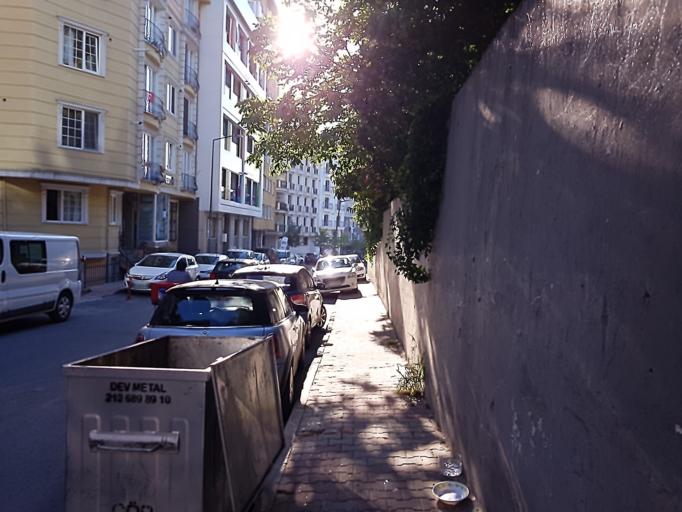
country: TR
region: Istanbul
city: Sisli
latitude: 41.0715
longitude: 29.0056
